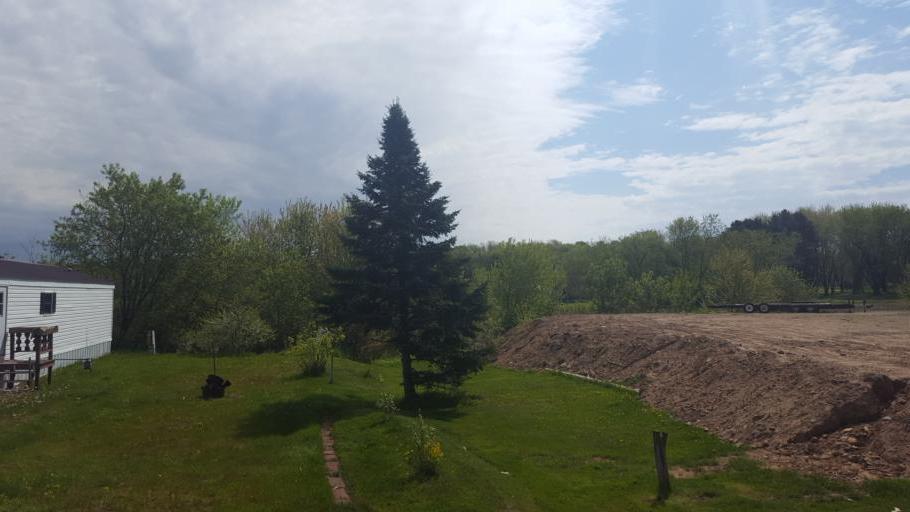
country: US
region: Wisconsin
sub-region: Clark County
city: Neillsville
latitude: 44.5841
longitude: -90.4588
